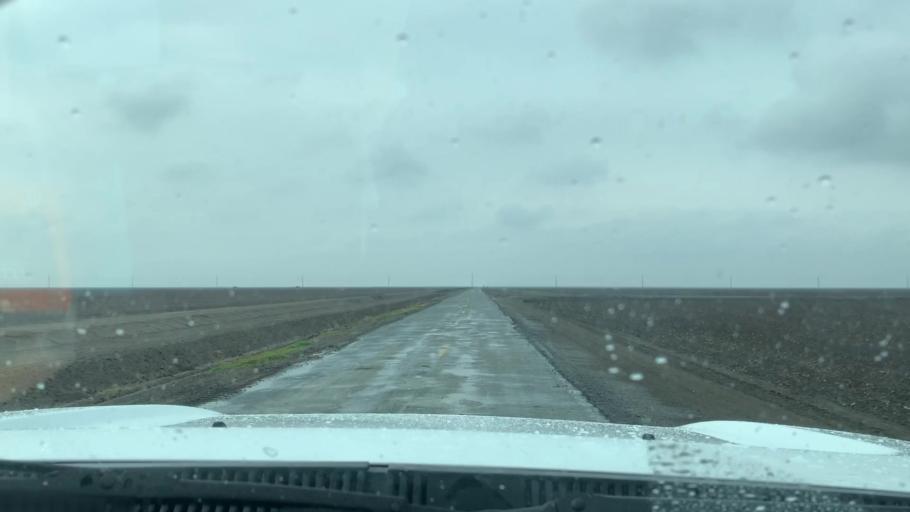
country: US
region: California
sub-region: Kings County
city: Corcoran
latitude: 36.0072
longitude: -119.5618
